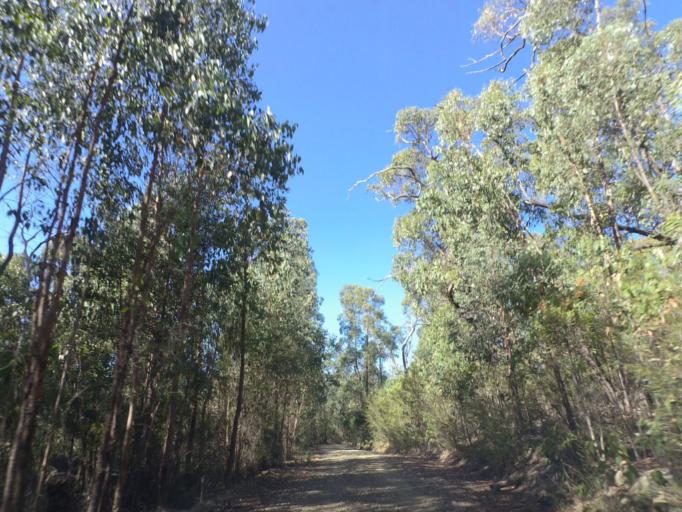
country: AU
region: Victoria
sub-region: Murrindindi
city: Kinglake West
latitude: -37.4613
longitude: 145.3872
